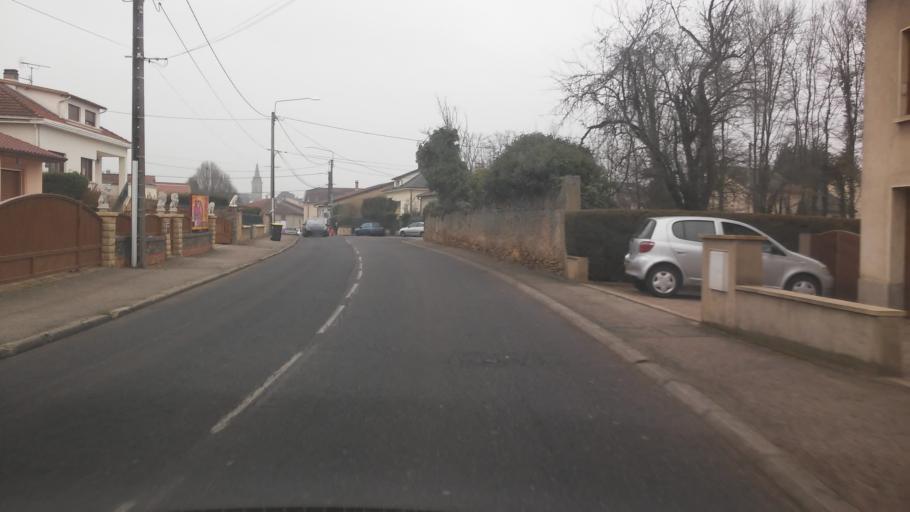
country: FR
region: Lorraine
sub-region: Departement de la Moselle
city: Augny
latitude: 49.0622
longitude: 6.1162
